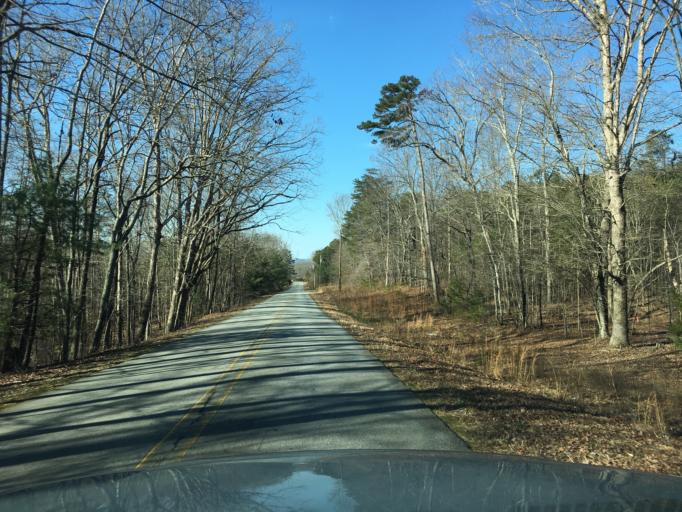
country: US
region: South Carolina
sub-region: Pickens County
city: Arial
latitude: 34.8737
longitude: -82.6560
